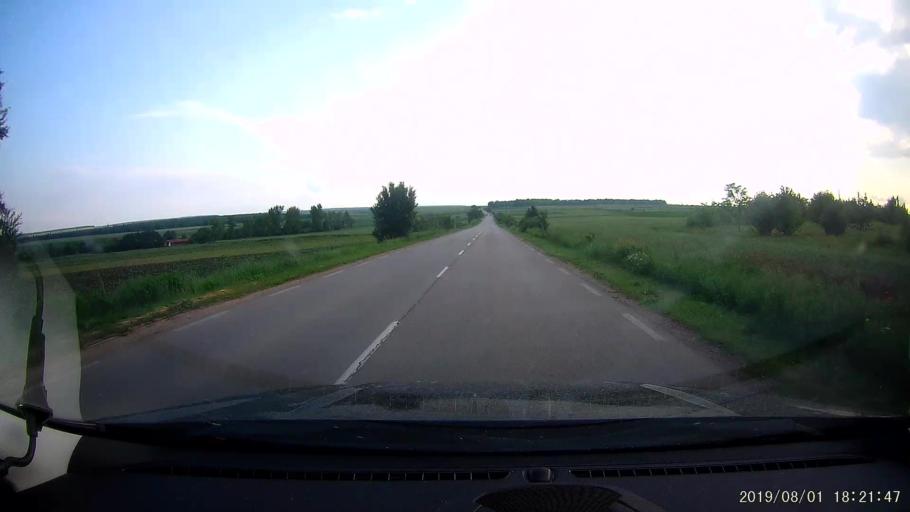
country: BG
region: Shumen
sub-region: Obshtina Kaolinovo
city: Kaolinovo
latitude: 43.6479
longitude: 27.0657
